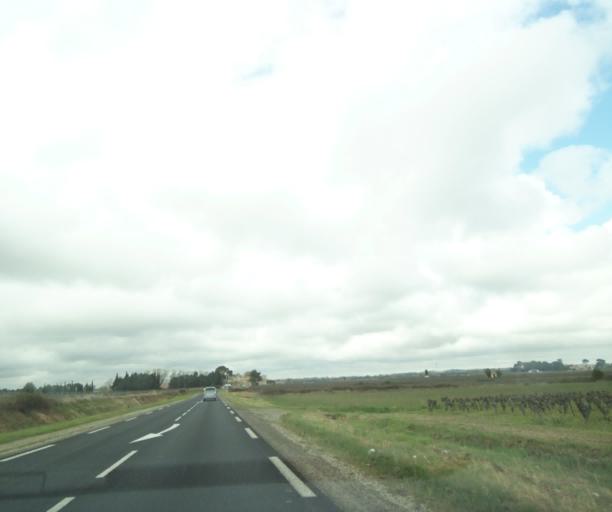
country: FR
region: Languedoc-Roussillon
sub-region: Departement de l'Herault
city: Pignan
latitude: 43.5917
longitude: 3.7731
